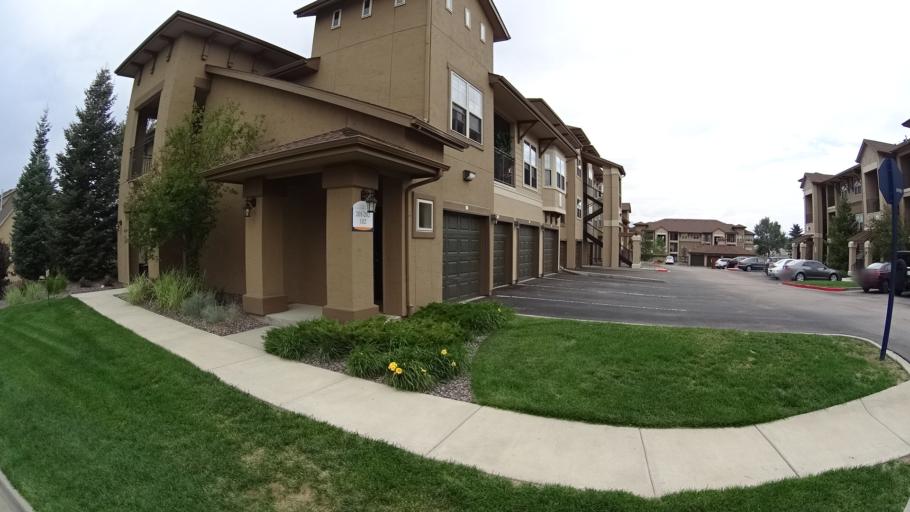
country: US
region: Colorado
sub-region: El Paso County
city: Gleneagle
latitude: 39.0030
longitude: -104.8000
